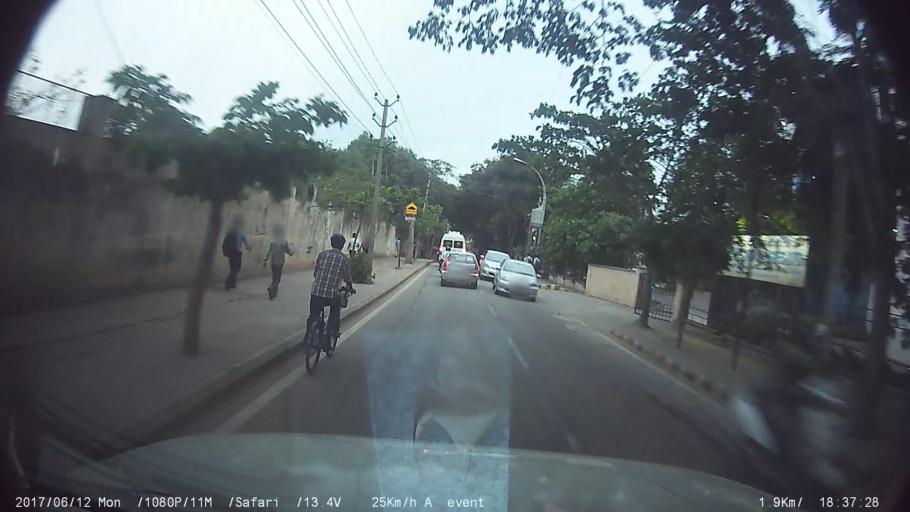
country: IN
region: Karnataka
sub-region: Bangalore Urban
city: Anekal
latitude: 12.8440
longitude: 77.6714
